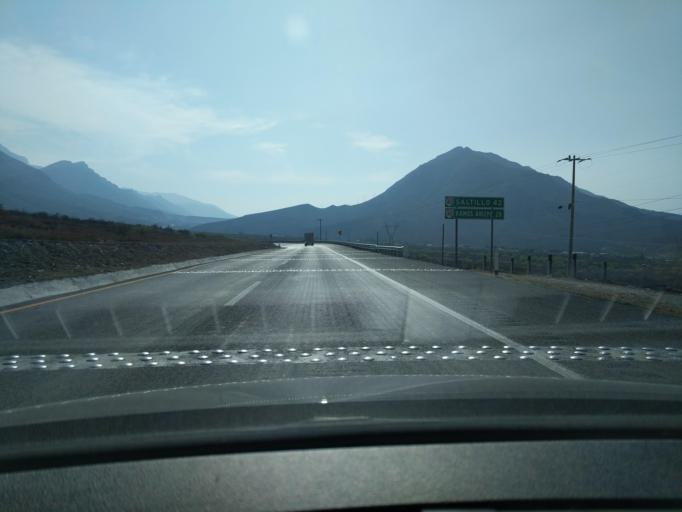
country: MX
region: Nuevo Leon
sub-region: Garcia
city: Las Torres de Guadalupe
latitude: 25.6685
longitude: -100.7038
